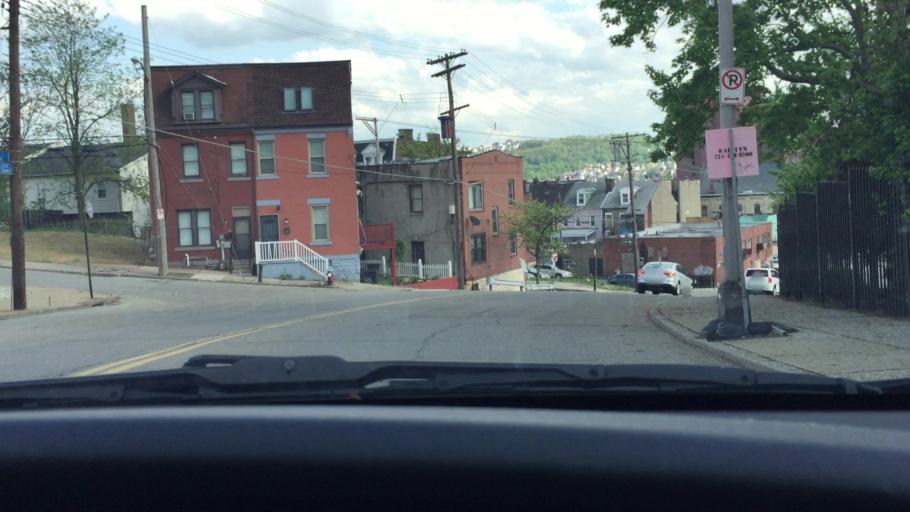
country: US
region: Pennsylvania
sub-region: Allegheny County
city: Pittsburgh
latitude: 40.4397
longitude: -79.9853
